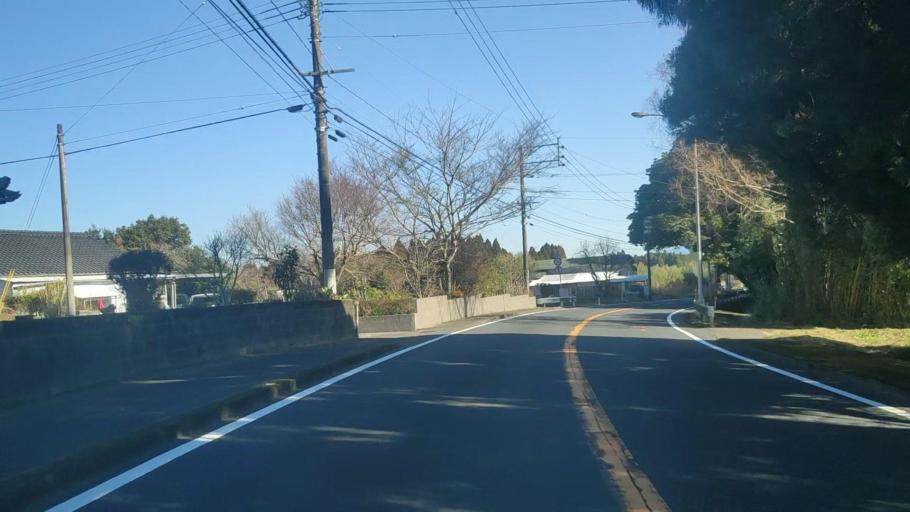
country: JP
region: Kagoshima
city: Sueyoshicho-ninokata
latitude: 31.6862
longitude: 130.9458
